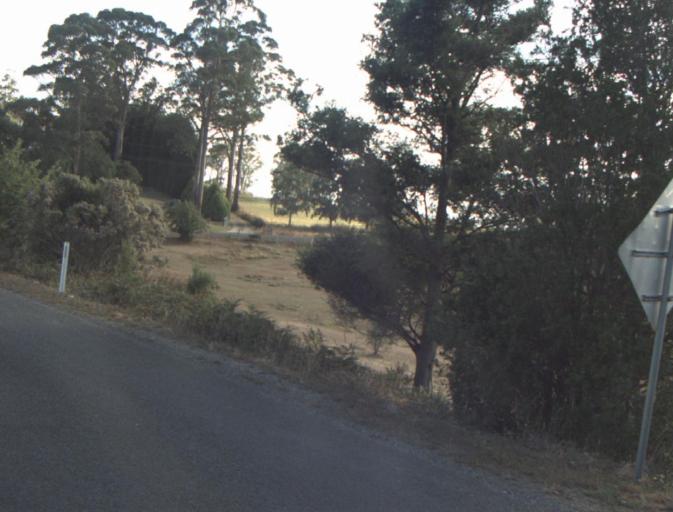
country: AU
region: Tasmania
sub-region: Launceston
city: Mayfield
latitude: -41.2080
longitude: 147.2151
